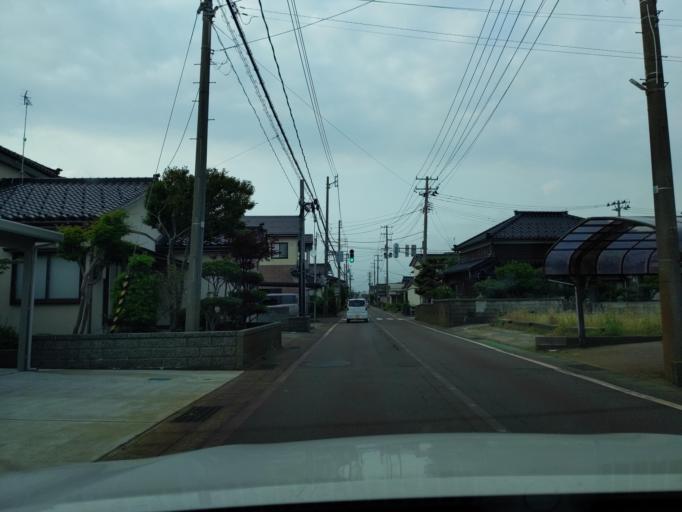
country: JP
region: Niigata
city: Kashiwazaki
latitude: 37.3860
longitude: 138.5778
